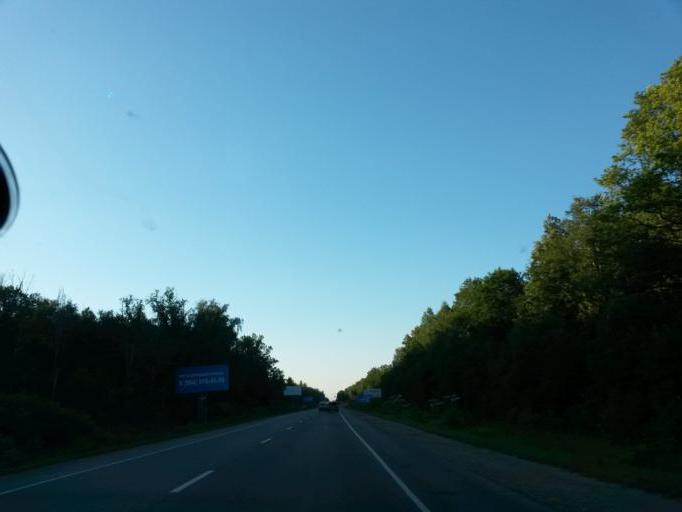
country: RU
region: Moskovskaya
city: Serpukhov
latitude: 54.9703
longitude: 37.4137
